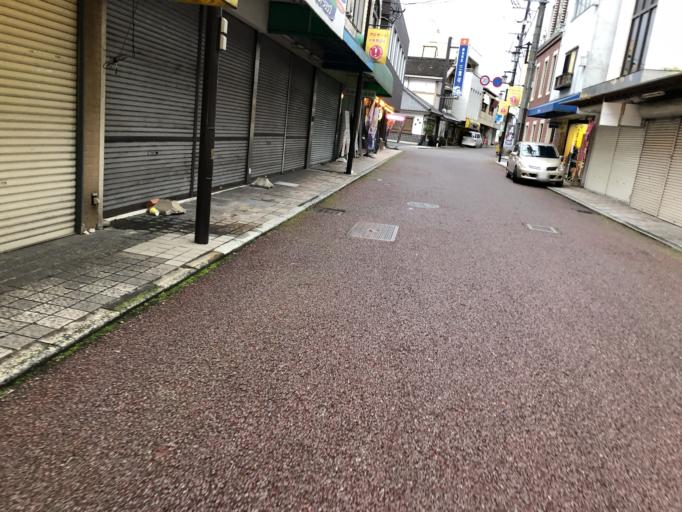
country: JP
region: Oita
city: Hita
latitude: 33.3183
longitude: 130.9371
